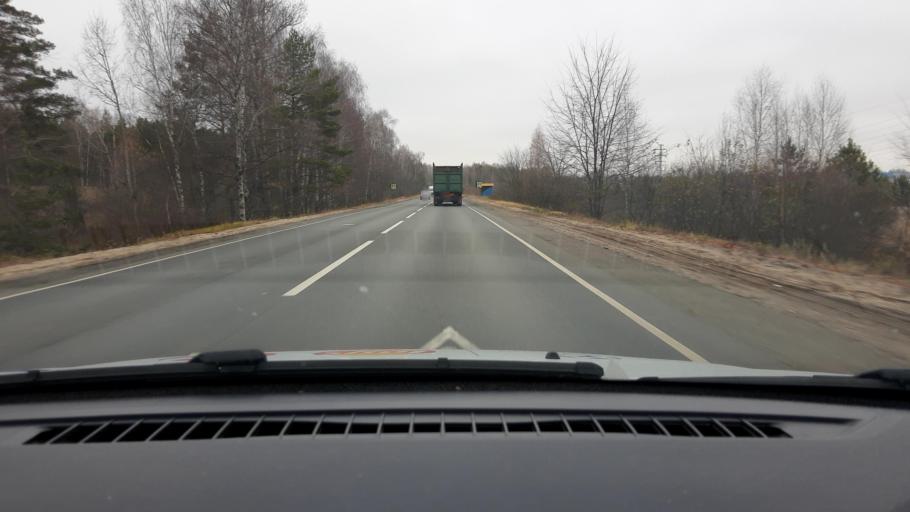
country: RU
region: Nizjnij Novgorod
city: Gorodets
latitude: 56.5626
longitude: 43.4923
